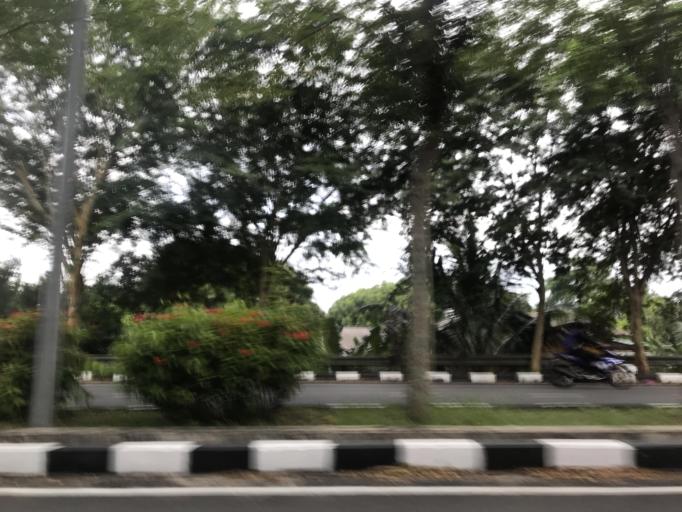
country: MY
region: Kelantan
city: Kota Bharu
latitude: 6.1109
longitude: 102.2349
